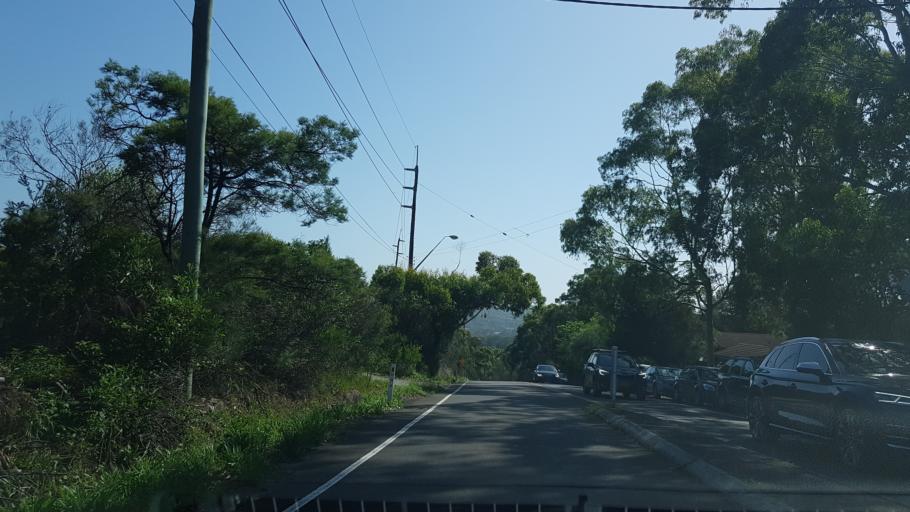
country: AU
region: New South Wales
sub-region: Warringah
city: Narraweena
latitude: -33.7441
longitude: 151.2658
